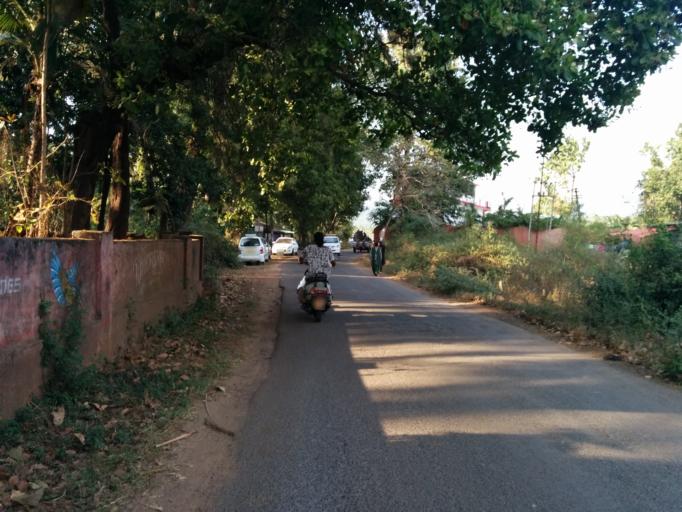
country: IN
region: Goa
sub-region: South Goa
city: Kankon
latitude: 15.0093
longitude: 74.0295
